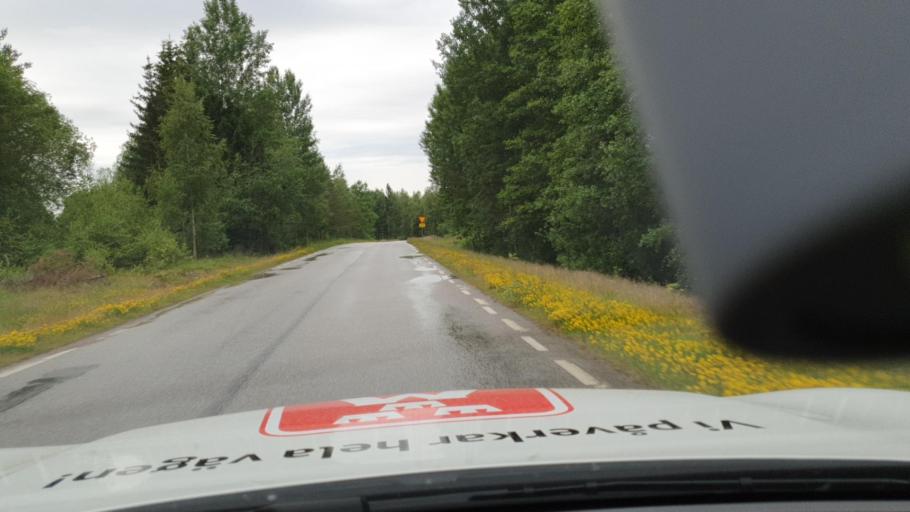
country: SE
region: Vaestra Goetaland
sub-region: Toreboda Kommun
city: Toereboda
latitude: 58.8298
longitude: 13.9935
